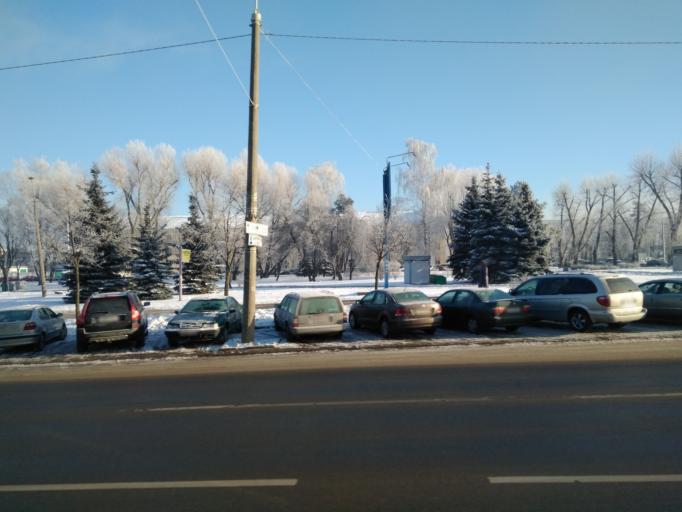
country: BY
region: Minsk
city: Minsk
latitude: 53.8910
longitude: 27.6133
